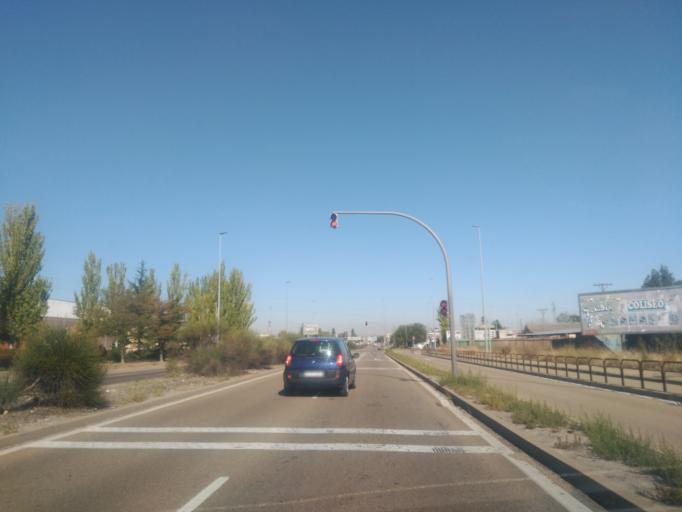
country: ES
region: Castille and Leon
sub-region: Provincia de Valladolid
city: Cisterniga
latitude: 41.6254
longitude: -4.6986
